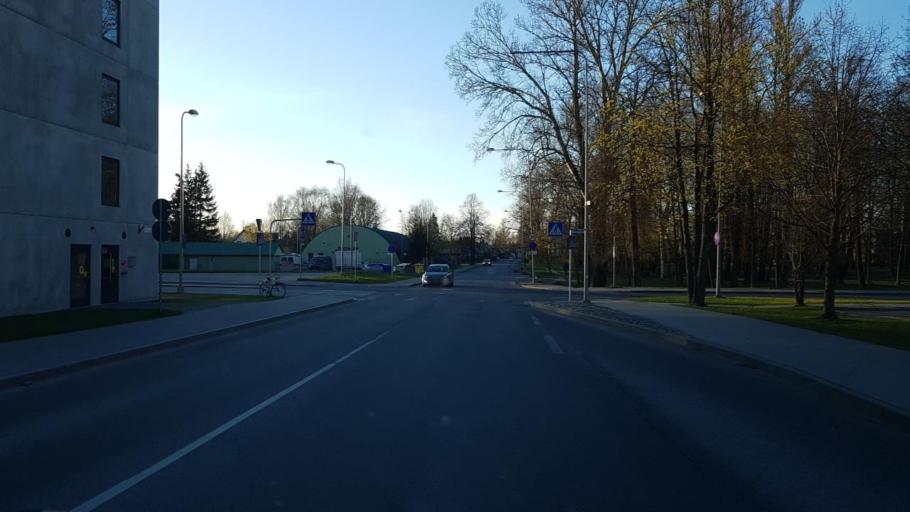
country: EE
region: Tartu
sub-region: Tartu linn
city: Tartu
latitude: 58.3700
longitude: 26.6982
